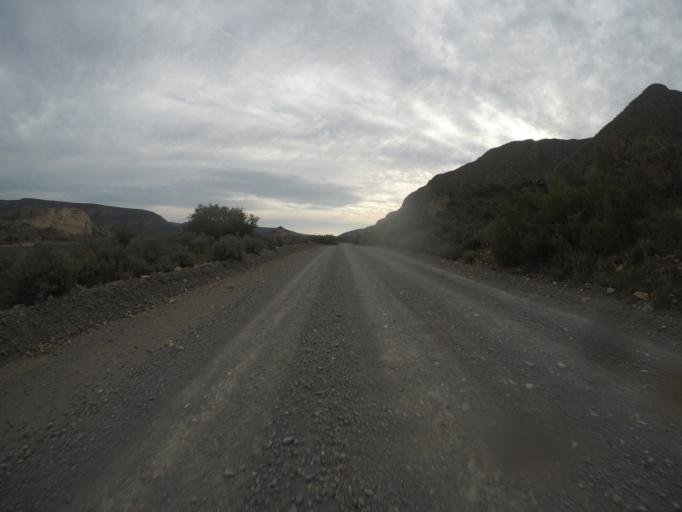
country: ZA
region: Eastern Cape
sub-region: Cacadu District Municipality
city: Willowmore
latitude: -33.5192
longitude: 23.6891
